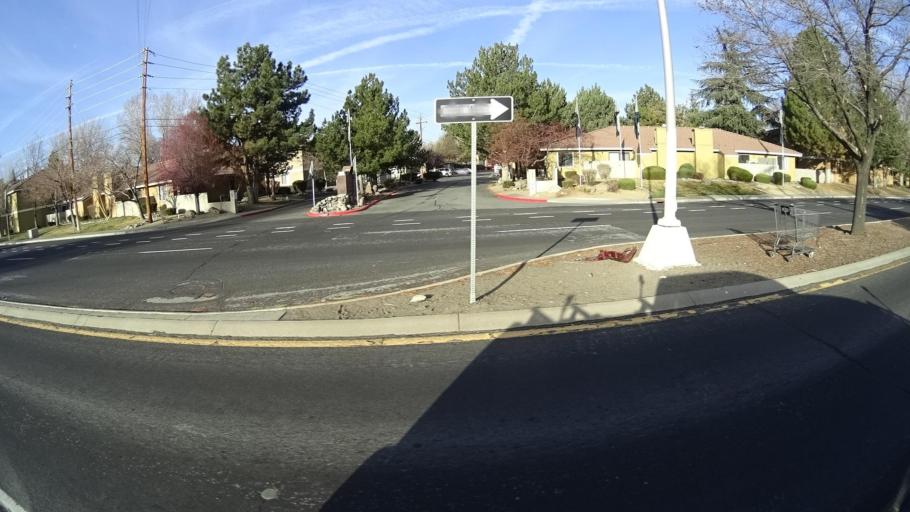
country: US
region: Nevada
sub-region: Washoe County
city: Sparks
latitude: 39.5493
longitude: -119.7760
